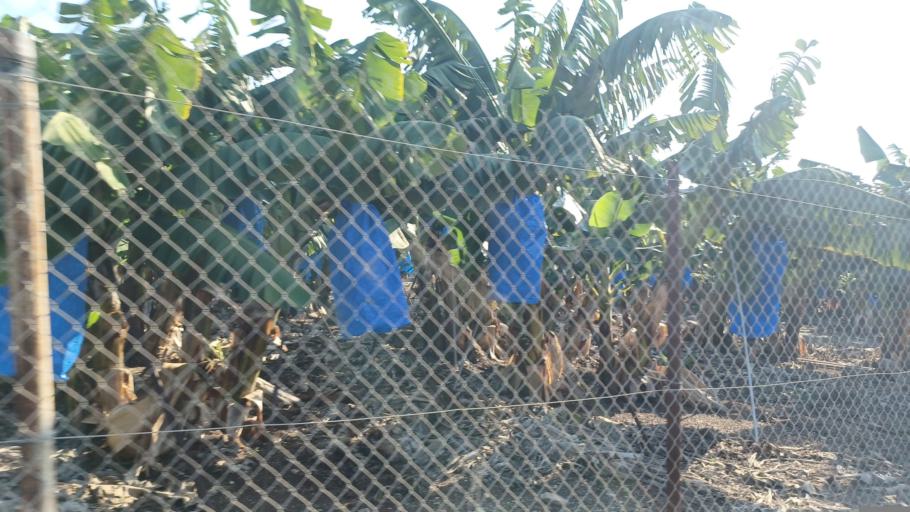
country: CY
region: Pafos
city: Kissonerga
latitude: 34.8395
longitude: 32.3914
